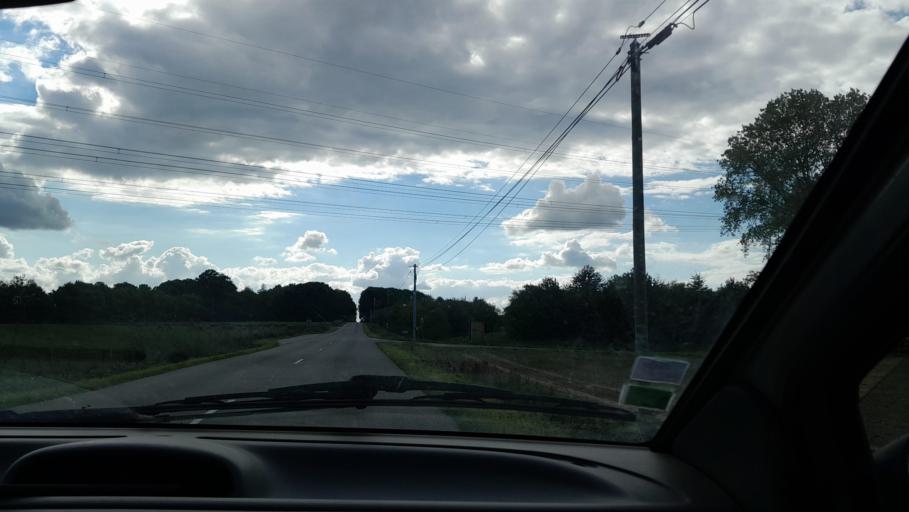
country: FR
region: Brittany
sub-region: Departement d'Ille-et-Vilaine
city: Le Pertre
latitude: 47.9854
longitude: -1.0009
